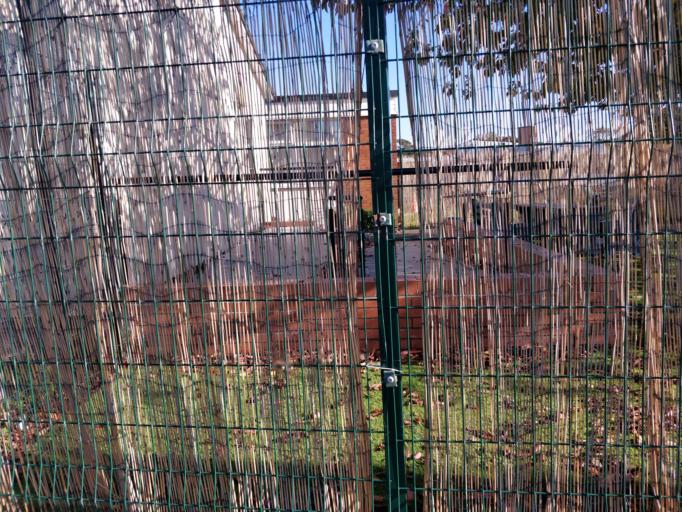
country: GB
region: England
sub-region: Sefton
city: Southport
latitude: 53.6665
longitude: -2.9635
